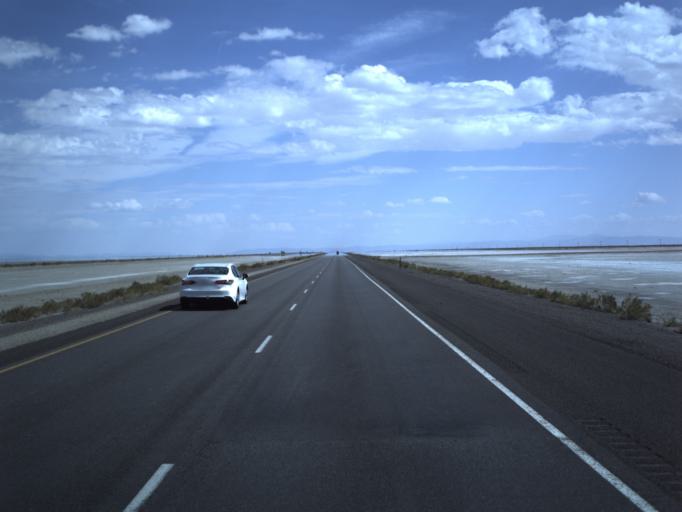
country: US
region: Utah
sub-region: Tooele County
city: Wendover
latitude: 40.7366
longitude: -113.7595
